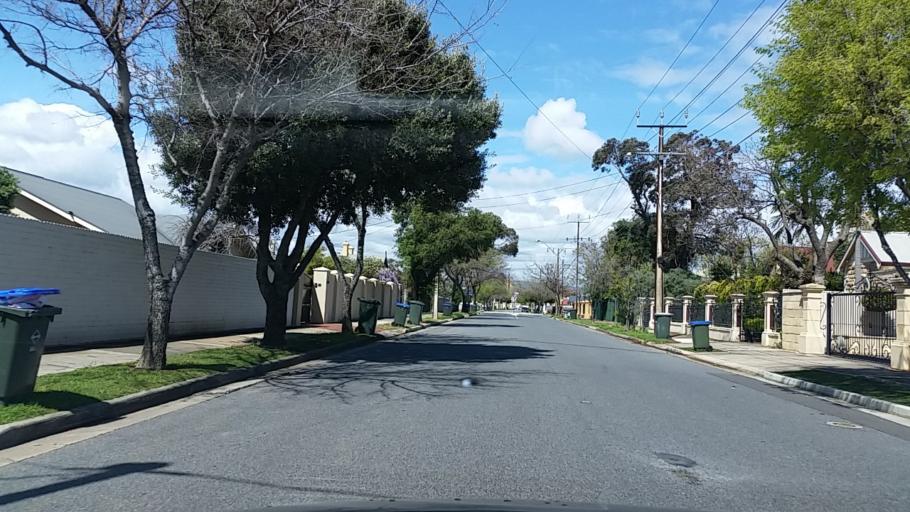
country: AU
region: South Australia
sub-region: Charles Sturt
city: Woodville North
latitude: -34.8778
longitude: 138.5444
